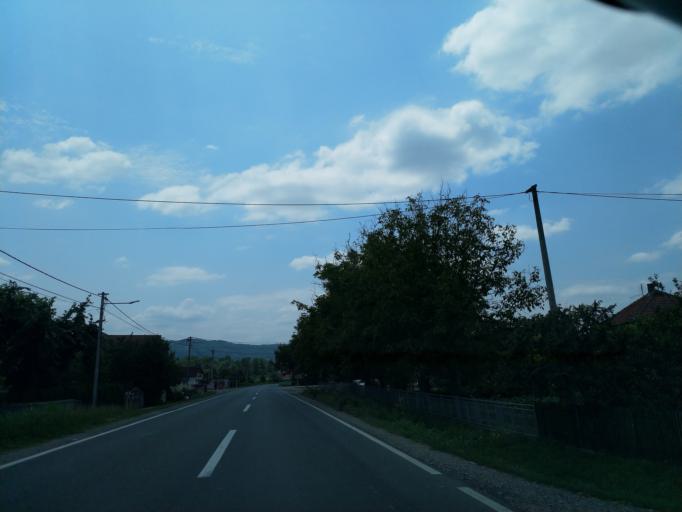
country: RS
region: Central Serbia
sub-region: Toplicki Okrug
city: Blace
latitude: 43.4432
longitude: 21.2270
